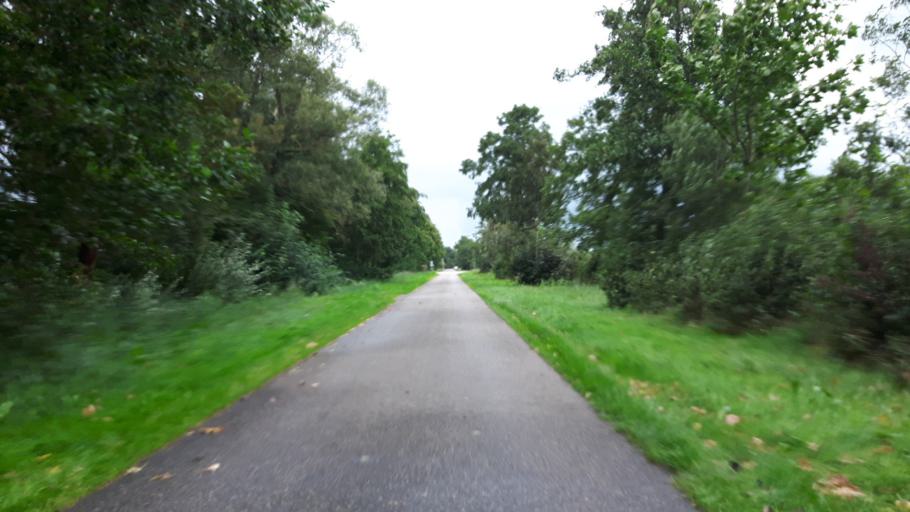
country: NL
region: Friesland
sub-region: Gemeente Dantumadiel
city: Broeksterwald
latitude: 53.2691
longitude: 5.9830
